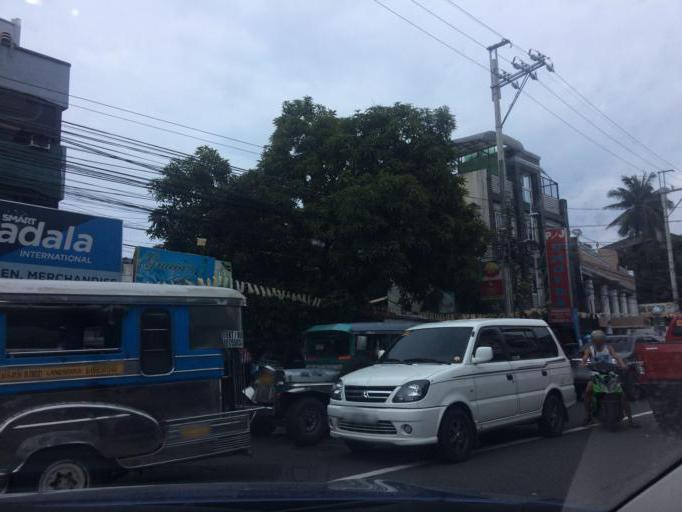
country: PH
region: Metro Manila
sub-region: Makati City
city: Makati City
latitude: 14.5480
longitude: 121.0020
